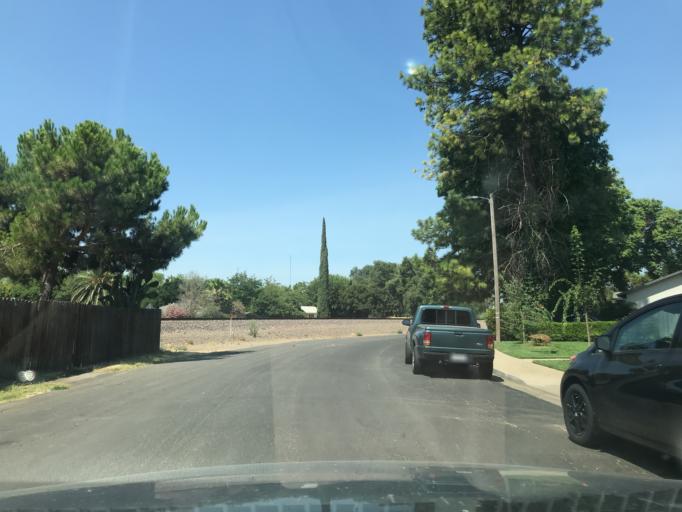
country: US
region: California
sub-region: Merced County
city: Merced
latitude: 37.3141
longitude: -120.4937
